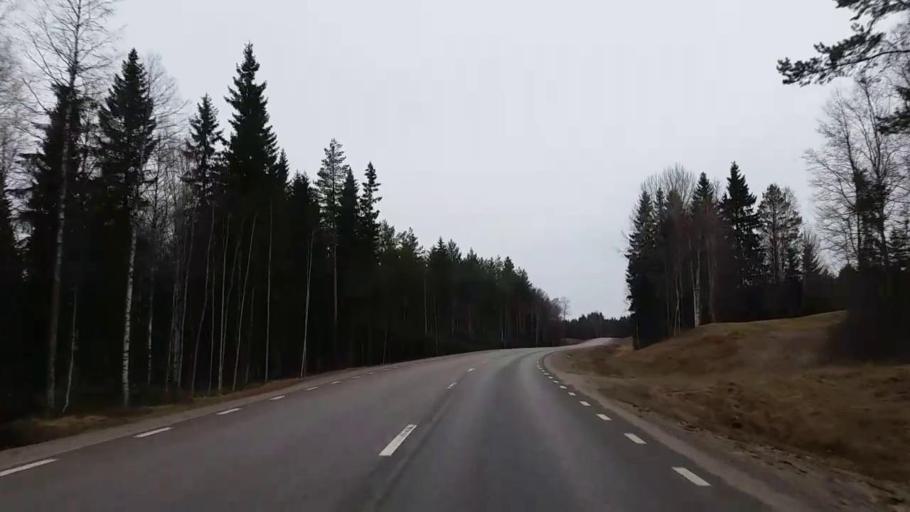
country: SE
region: Gaevleborg
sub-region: Ovanakers Kommun
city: Edsbyn
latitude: 61.1955
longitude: 15.8739
